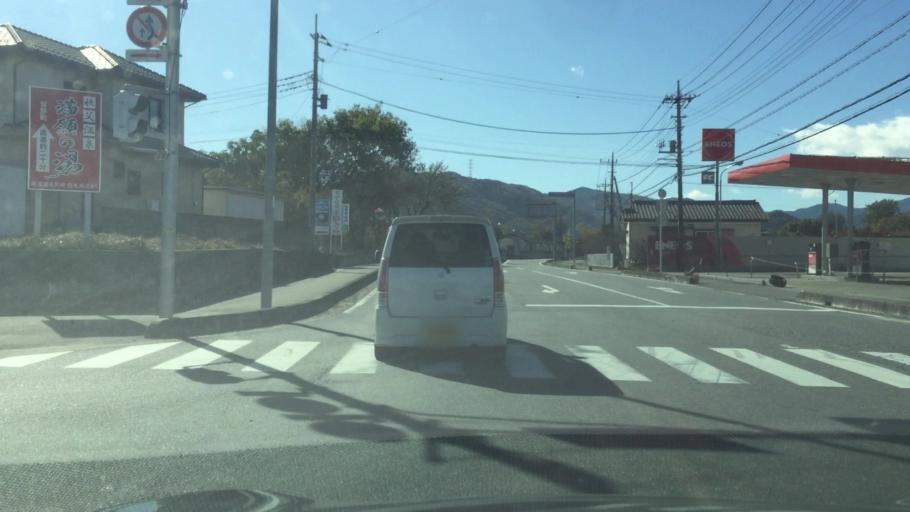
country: JP
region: Saitama
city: Kodamacho-kodamaminami
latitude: 36.1824
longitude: 139.1242
